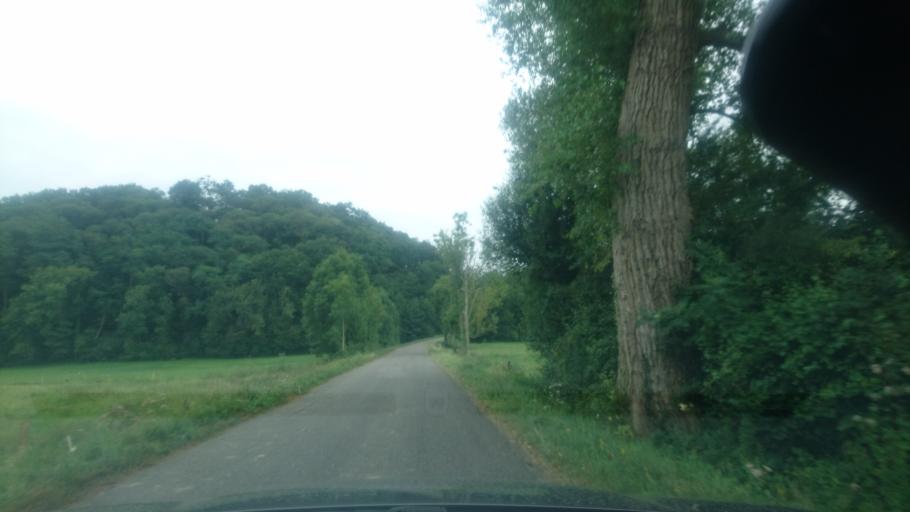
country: FR
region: Midi-Pyrenees
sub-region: Departement des Hautes-Pyrenees
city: Odos
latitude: 43.1467
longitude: 0.0444
